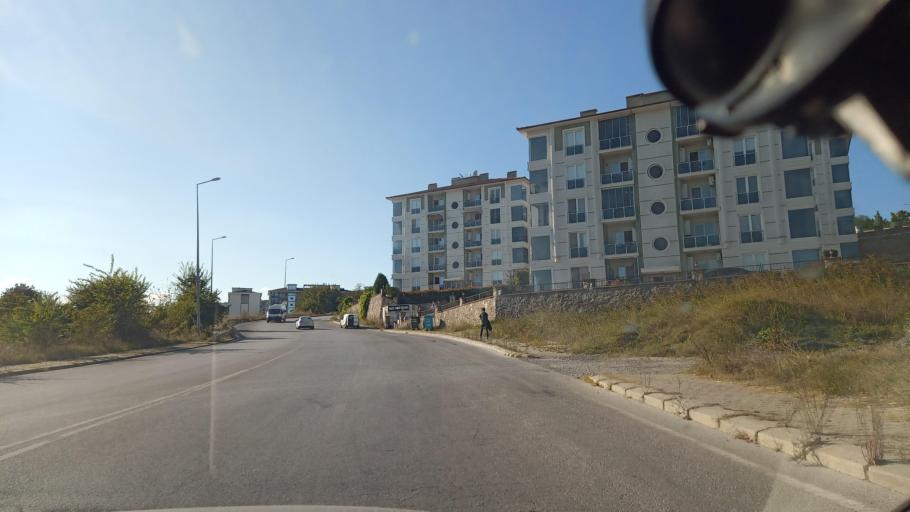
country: TR
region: Sakarya
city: Kazimpasa
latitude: 40.8545
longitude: 30.2926
